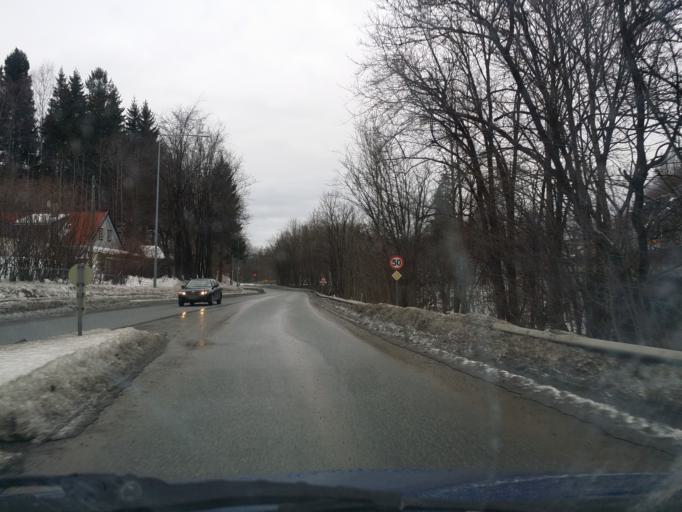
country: NO
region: Akershus
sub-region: Asker
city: Billingstad
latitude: 59.9010
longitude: 10.4948
